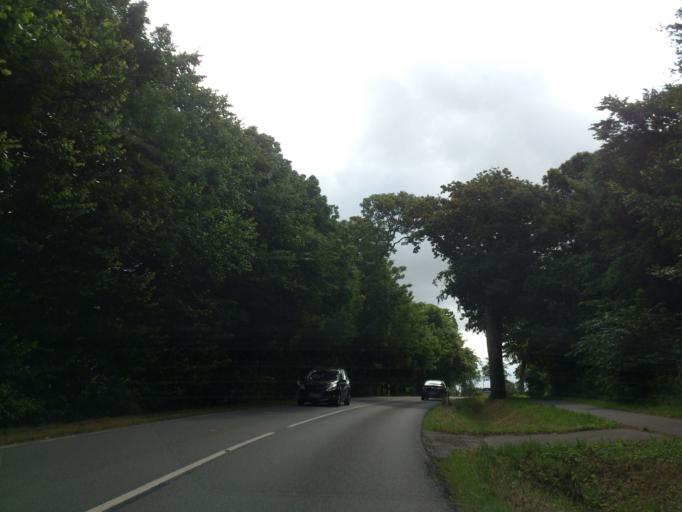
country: DE
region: Schleswig-Holstein
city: Sankt Peter-Ording
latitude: 54.3028
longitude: 8.6643
